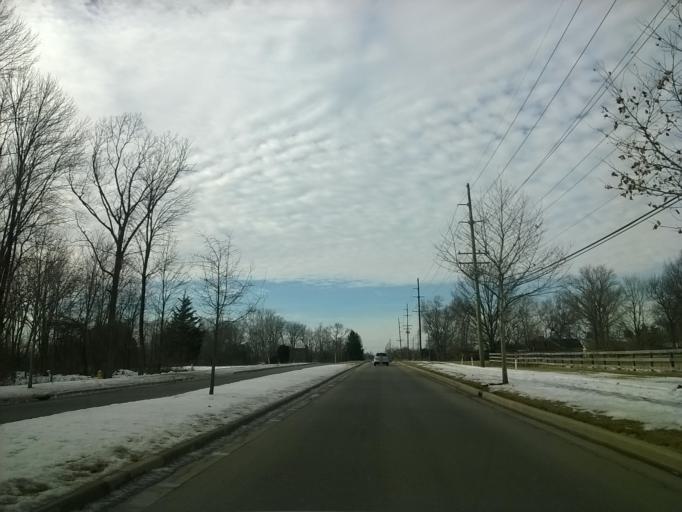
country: US
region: Indiana
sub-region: Hamilton County
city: Carmel
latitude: 39.9777
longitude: -86.1750
